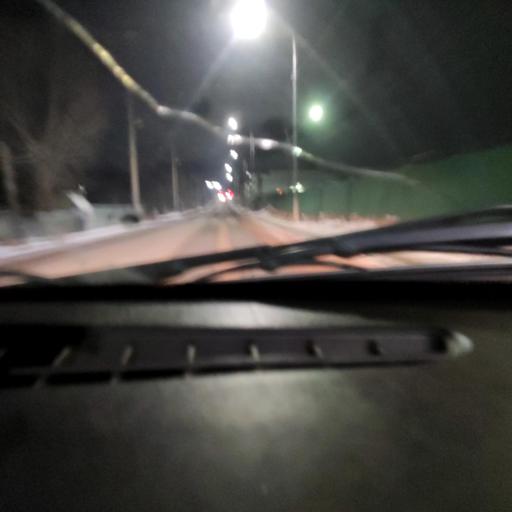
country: RU
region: Bashkortostan
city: Avdon
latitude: 54.6086
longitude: 55.8432
